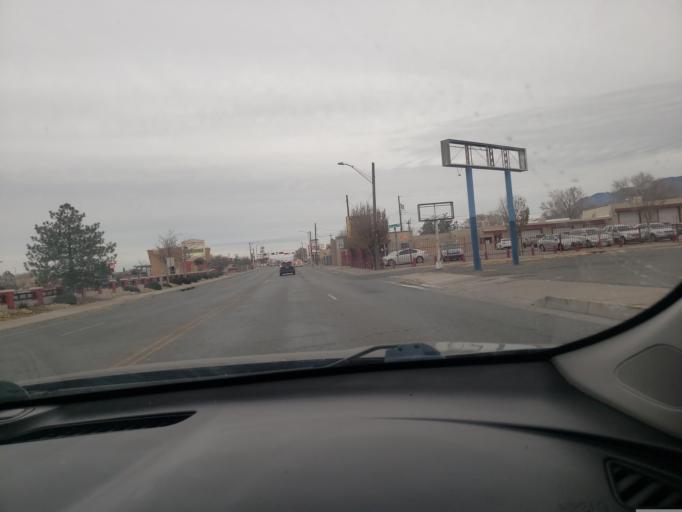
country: US
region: New Mexico
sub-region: Bernalillo County
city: Albuquerque
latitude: 35.0744
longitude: -106.5775
